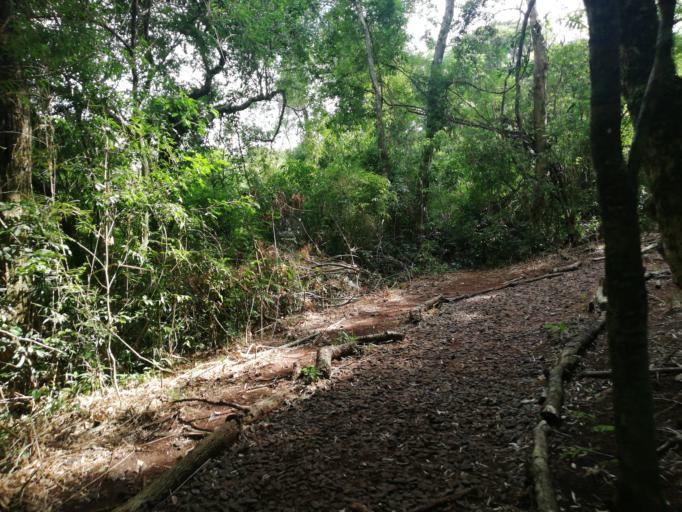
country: AR
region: Misiones
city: Cerro Azul
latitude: -27.6299
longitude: -55.4931
